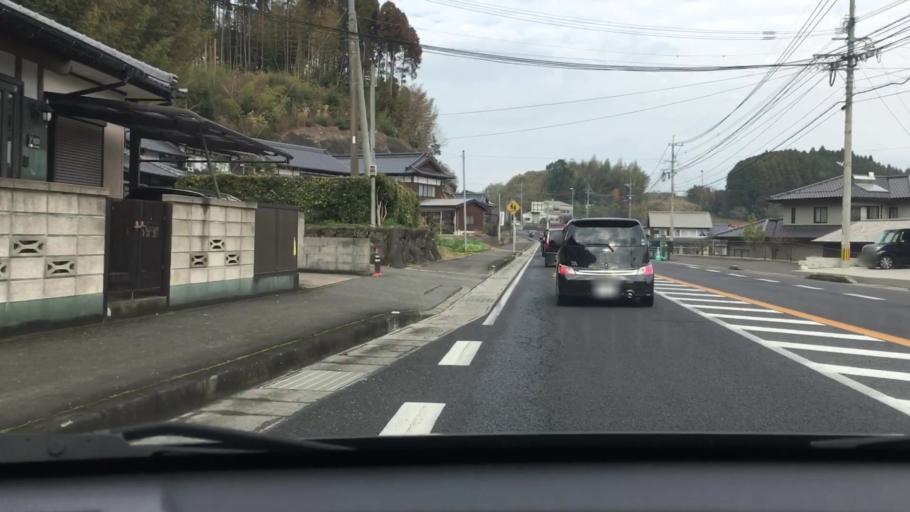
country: JP
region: Saga Prefecture
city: Imaricho-ko
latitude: 33.3075
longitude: 129.9265
